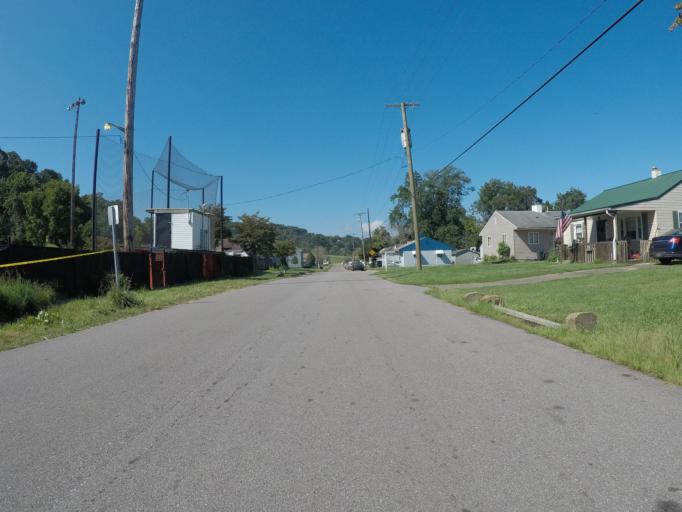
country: US
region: Ohio
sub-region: Lawrence County
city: Burlington
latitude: 38.3984
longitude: -82.5124
